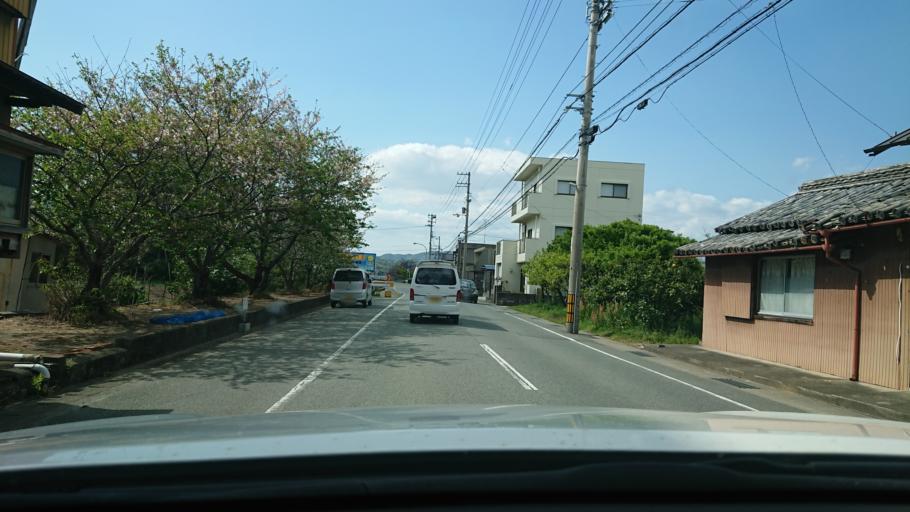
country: JP
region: Tokushima
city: Komatsushimacho
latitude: 34.0205
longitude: 134.5539
